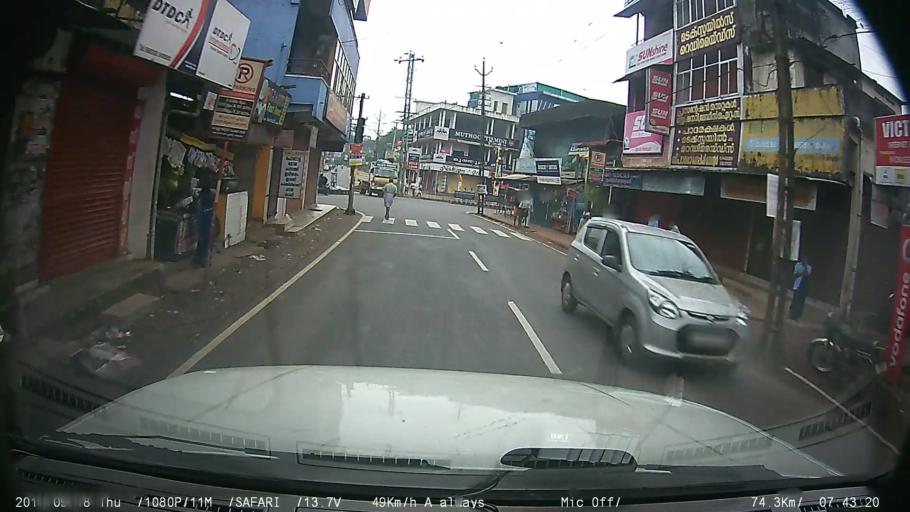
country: IN
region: Kerala
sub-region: Kottayam
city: Changanacheri
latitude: 9.4740
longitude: 76.5772
